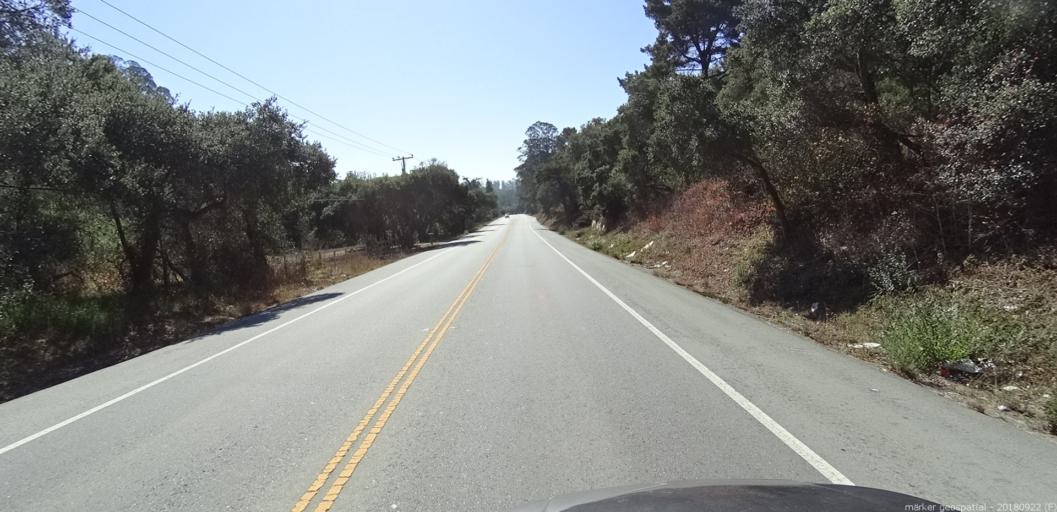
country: US
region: California
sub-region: Monterey County
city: Prunedale
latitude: 36.8272
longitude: -121.6769
